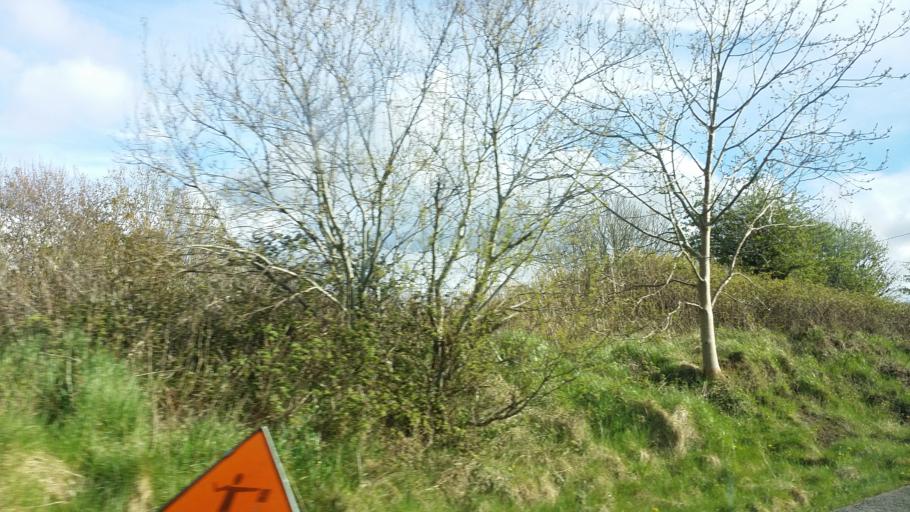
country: IE
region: Ulster
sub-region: County Donegal
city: Bundoran
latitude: 54.4684
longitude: -8.2777
